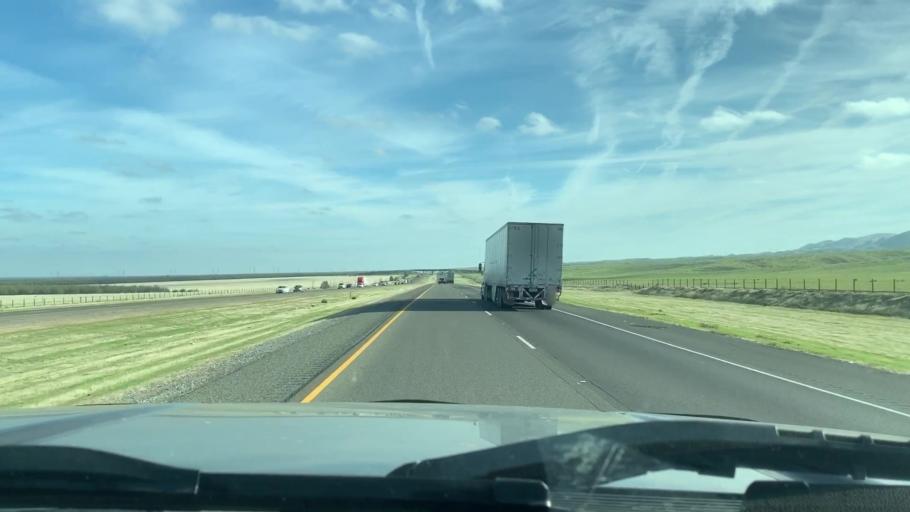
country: US
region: California
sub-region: Fresno County
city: Mendota
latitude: 36.5625
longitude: -120.5304
